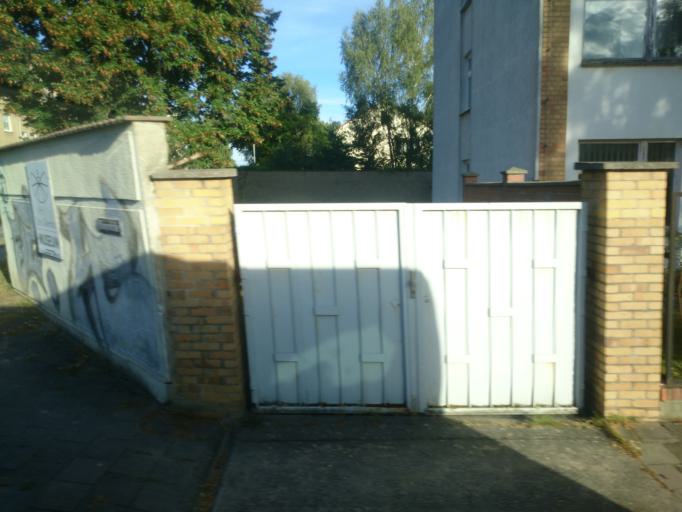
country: DE
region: Mecklenburg-Vorpommern
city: Anklam
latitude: 53.8534
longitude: 13.7034
